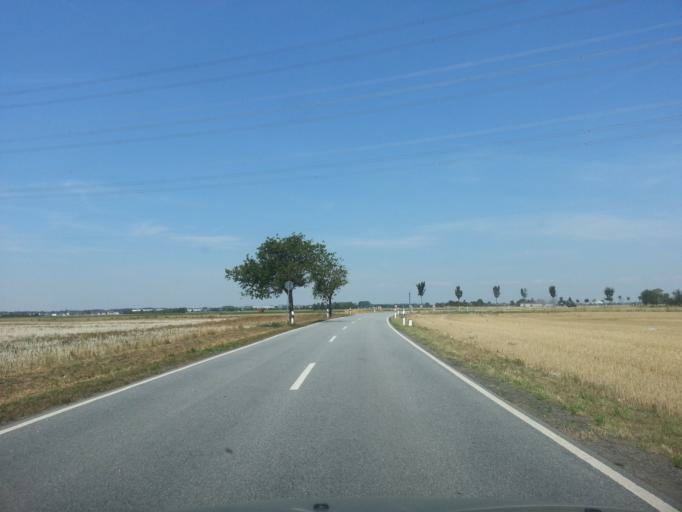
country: DE
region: Hesse
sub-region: Regierungsbezirk Darmstadt
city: Gross-Rohrheim
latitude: 49.7070
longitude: 8.5084
